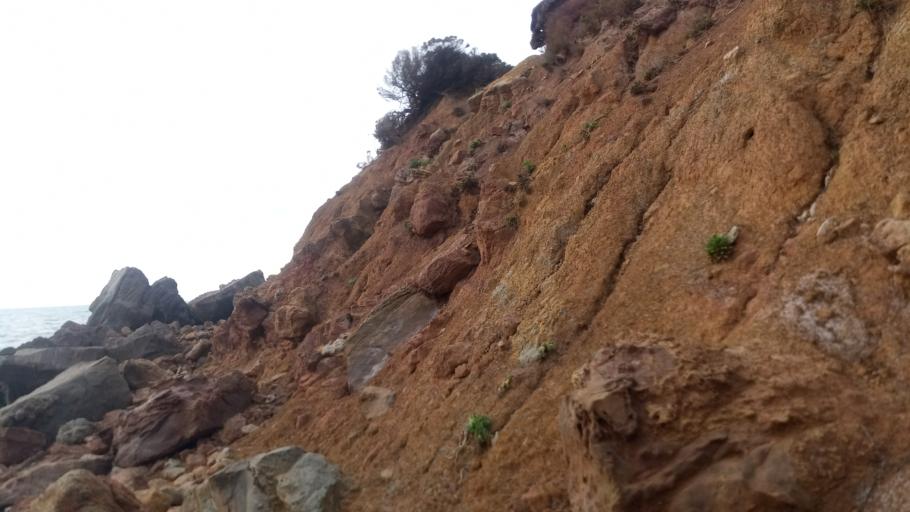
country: PT
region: Leiria
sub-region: Caldas da Rainha
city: Caldas da Rainha
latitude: 39.4906
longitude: -9.1804
